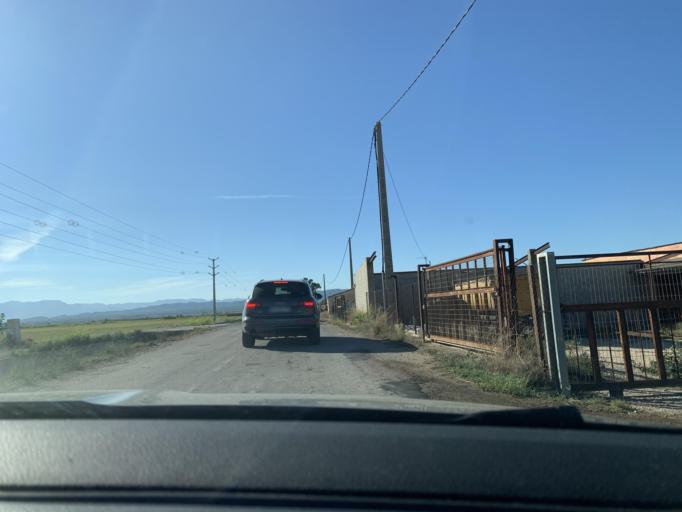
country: ES
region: Catalonia
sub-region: Provincia de Tarragona
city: Deltebre
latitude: 40.7504
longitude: 0.7241
